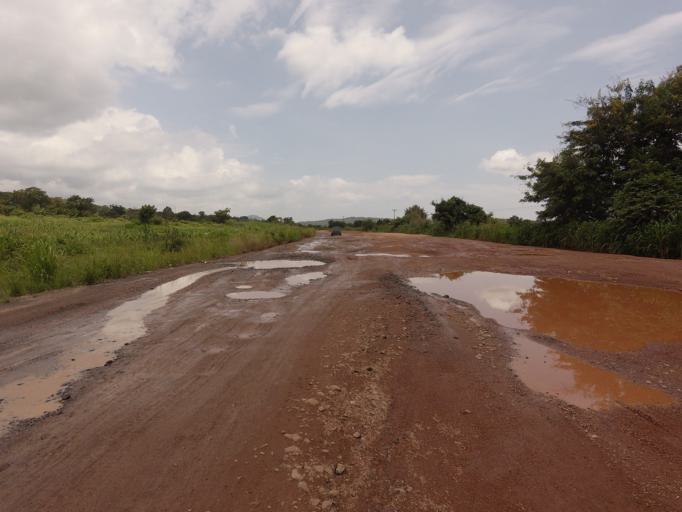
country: GH
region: Volta
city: Ho
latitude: 6.6785
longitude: 0.3168
